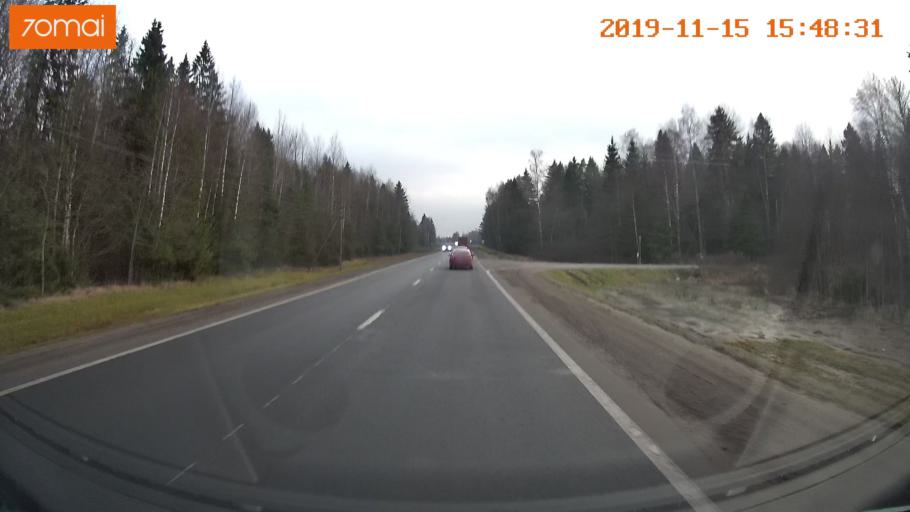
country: RU
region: Jaroslavl
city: Danilov
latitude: 57.9263
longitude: 40.0065
